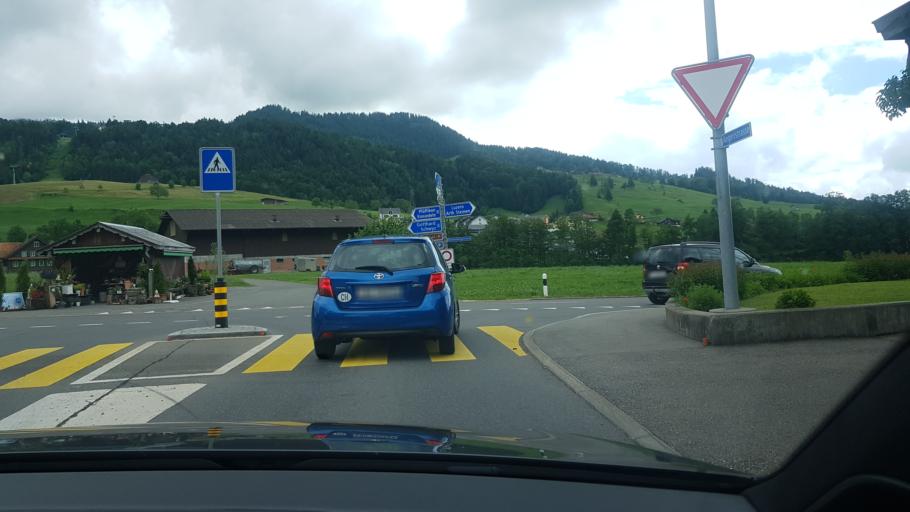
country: CH
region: Schwyz
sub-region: Bezirk Schwyz
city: Sattel
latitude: 47.0795
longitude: 8.6305
